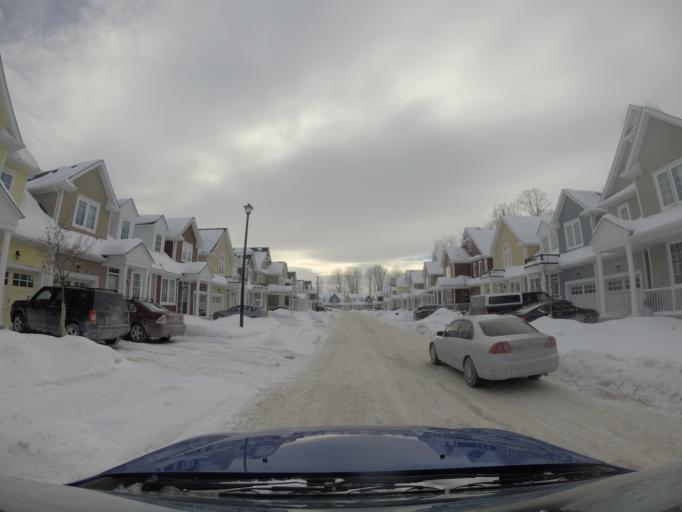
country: CA
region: Ontario
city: Wasaga Beach
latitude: 44.5297
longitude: -79.9856
